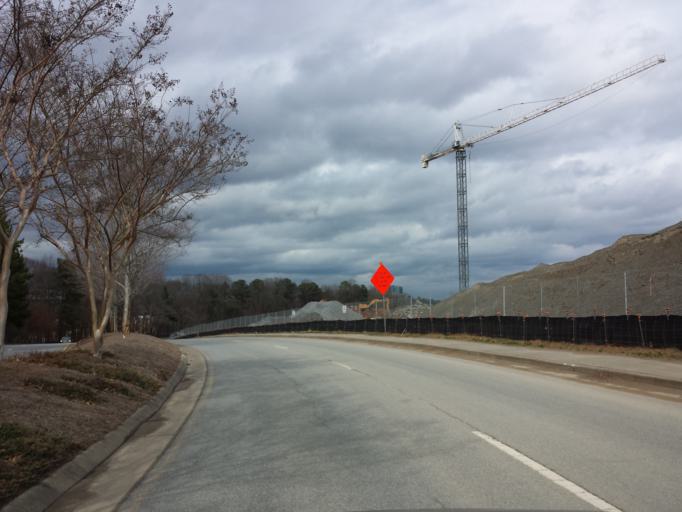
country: US
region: Georgia
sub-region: Cobb County
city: Vinings
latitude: 33.8900
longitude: -84.4704
